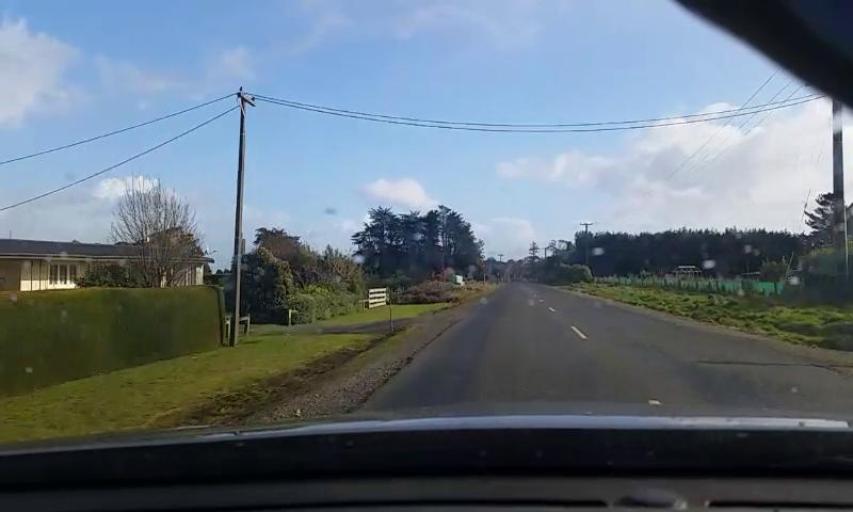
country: NZ
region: Southland
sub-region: Invercargill City
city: Invercargill
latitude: -46.3581
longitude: 168.3304
